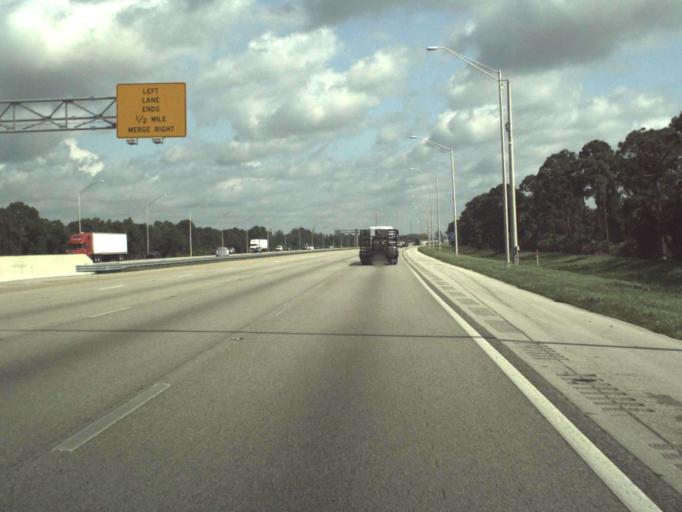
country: US
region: Florida
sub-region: Palm Beach County
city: Limestone Creek
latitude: 26.9168
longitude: -80.1446
